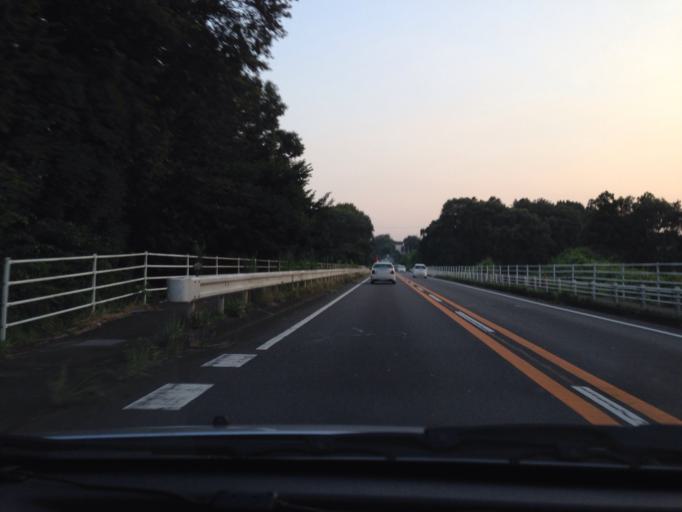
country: JP
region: Ibaraki
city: Ishioka
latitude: 36.1553
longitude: 140.2419
